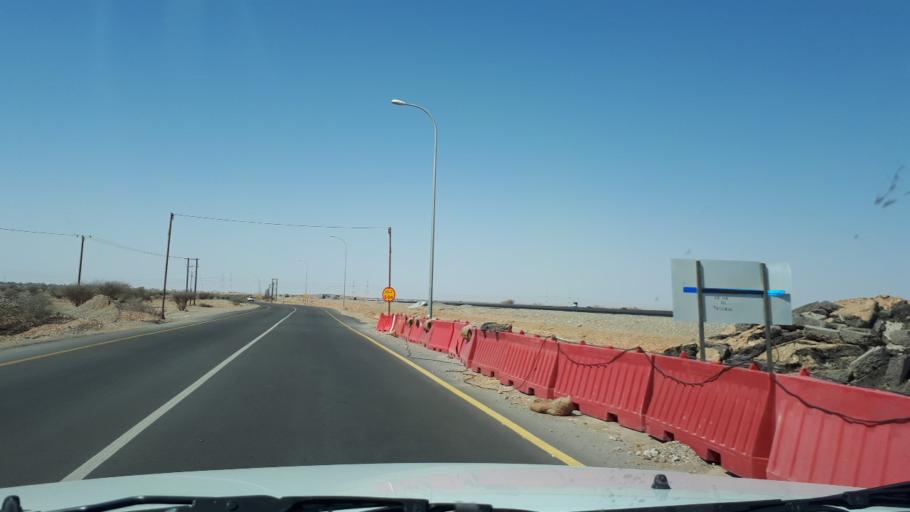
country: OM
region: Ash Sharqiyah
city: Sur
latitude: 22.2947
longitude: 59.2787
